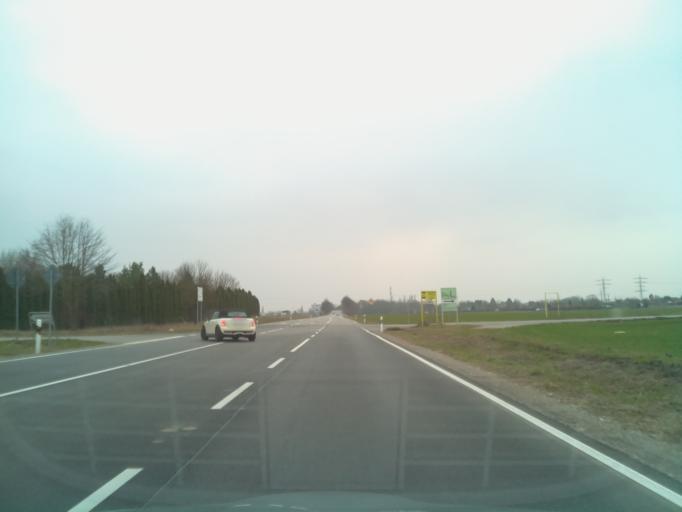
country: DE
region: Baden-Wuerttemberg
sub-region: Karlsruhe Region
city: Heddesheim
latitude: 49.4917
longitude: 8.6021
